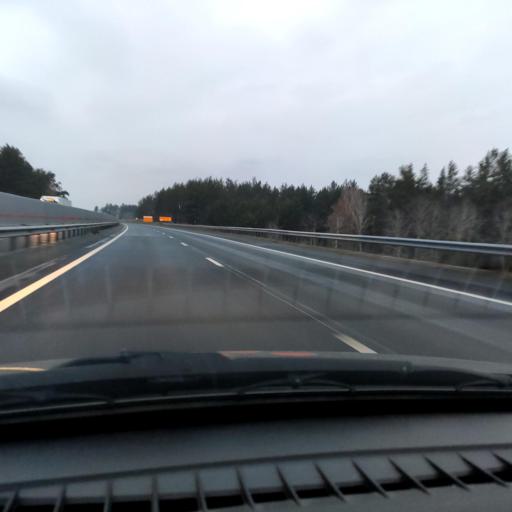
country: RU
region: Samara
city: Bereza
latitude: 53.4951
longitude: 50.0963
